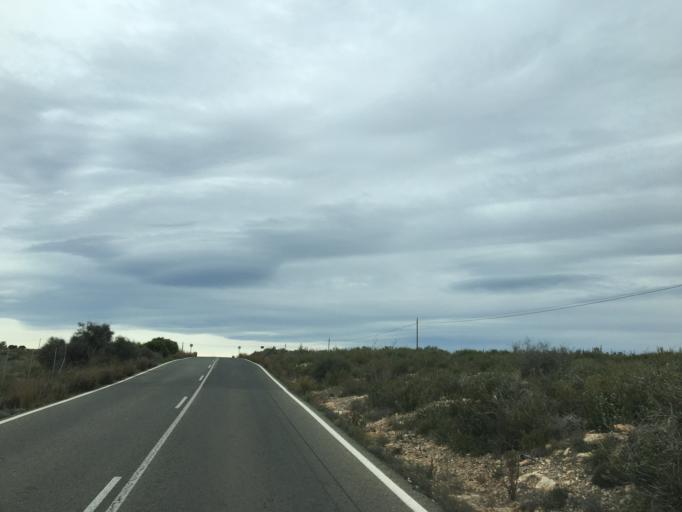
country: ES
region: Murcia
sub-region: Murcia
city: Cartagena
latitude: 37.6182
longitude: -1.0716
